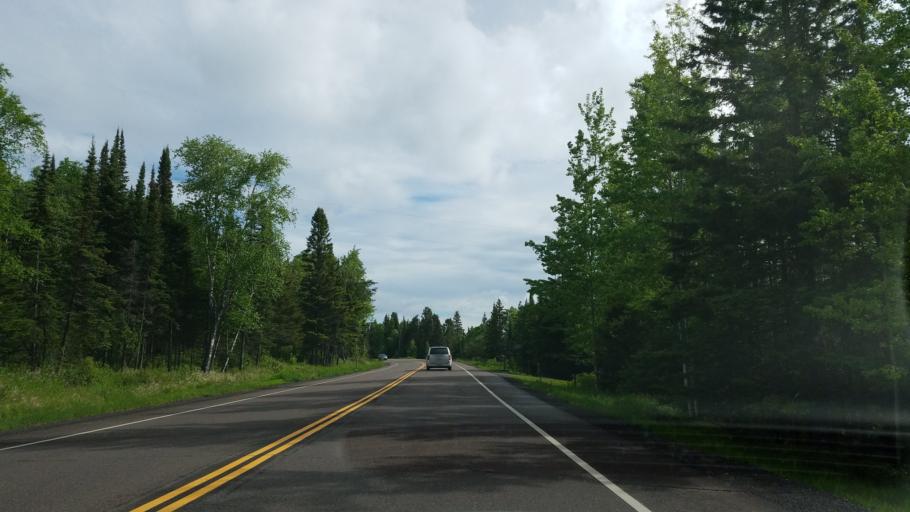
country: US
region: Minnesota
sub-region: Lake County
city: Two Harbors
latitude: 47.0737
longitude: -91.5880
